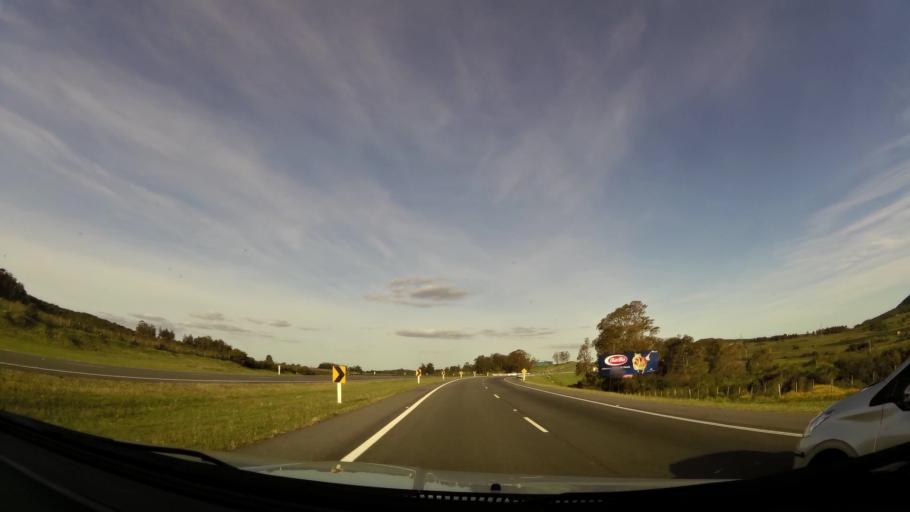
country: UY
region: Maldonado
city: Pan de Azucar
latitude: -34.7858
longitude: -55.2767
